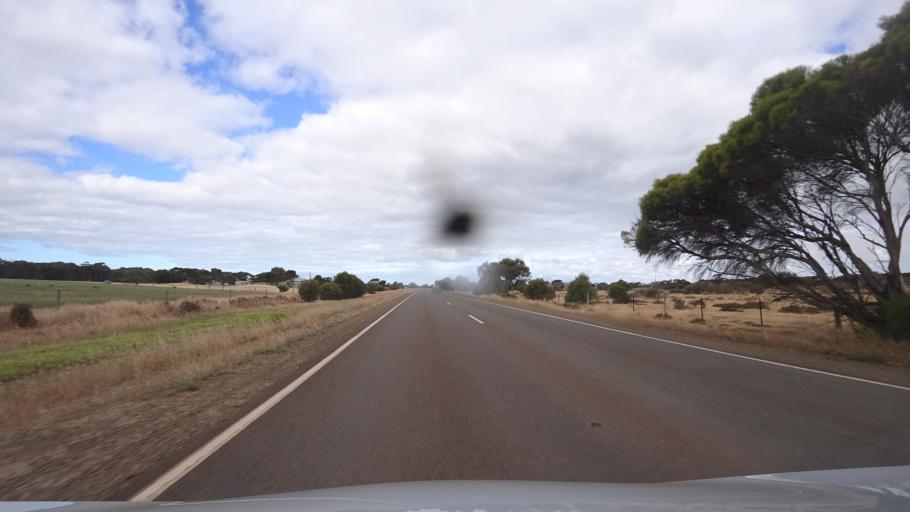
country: AU
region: South Australia
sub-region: Kangaroo Island
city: Kingscote
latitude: -35.6795
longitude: 137.5675
